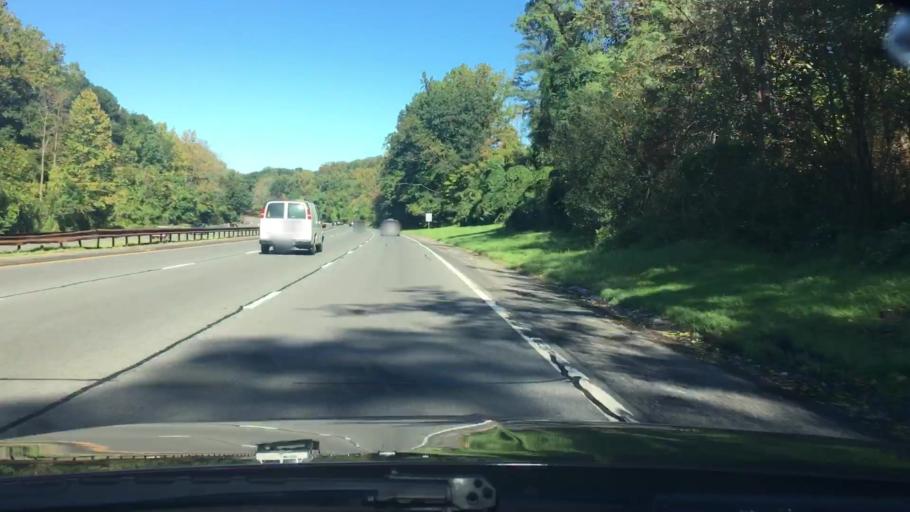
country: US
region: New York
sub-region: Westchester County
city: Ardsley
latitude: 41.0195
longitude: -73.8229
